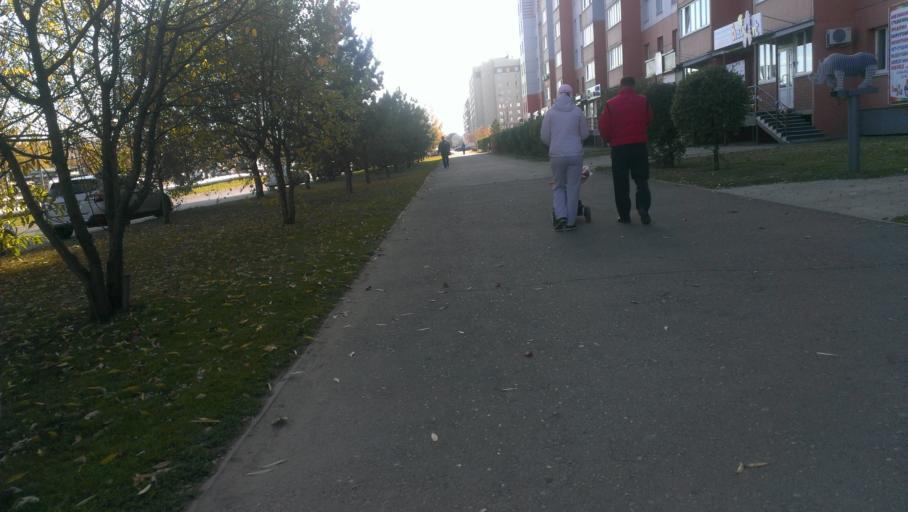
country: RU
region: Altai Krai
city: Novosilikatnyy
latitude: 53.3356
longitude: 83.6932
